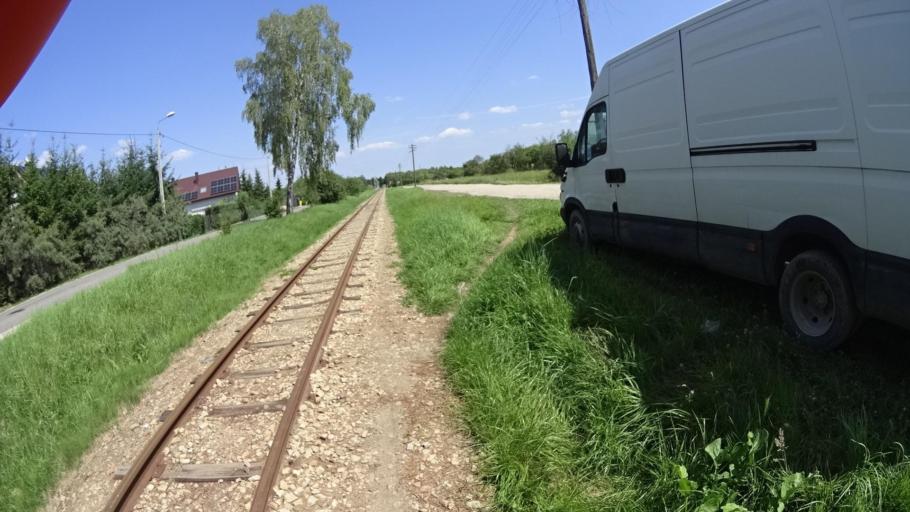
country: PL
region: Masovian Voivodeship
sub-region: Powiat piaseczynski
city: Lesznowola
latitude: 52.0241
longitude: 20.9422
